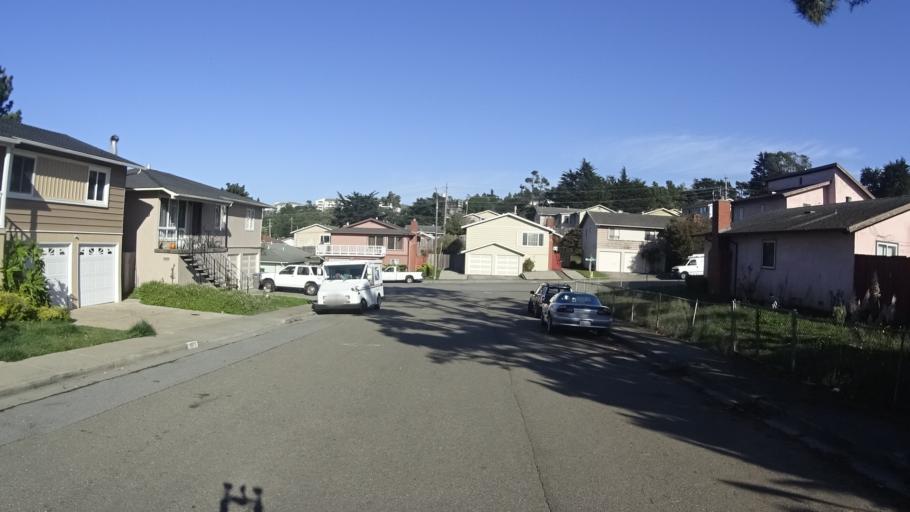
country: US
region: California
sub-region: San Mateo County
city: Pacifica
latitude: 37.6338
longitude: -122.4707
